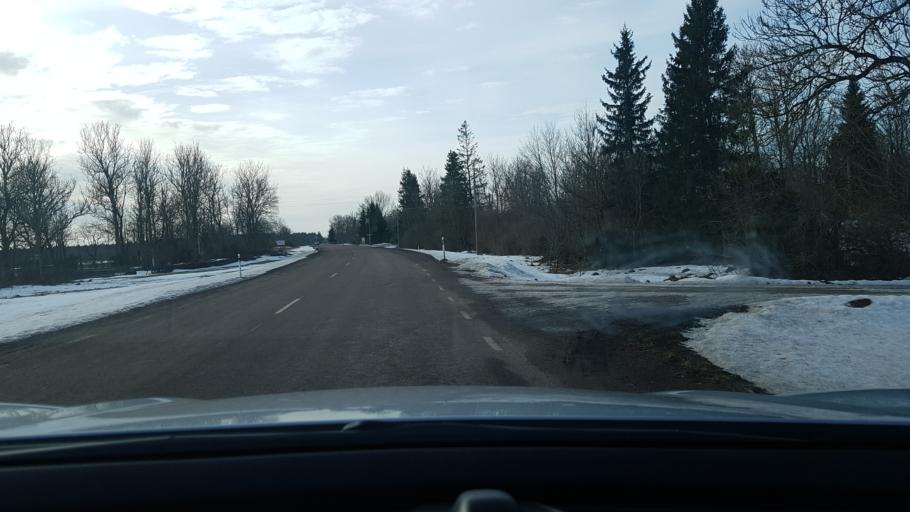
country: EE
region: Saare
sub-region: Kuressaare linn
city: Kuressaare
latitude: 58.3301
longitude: 22.5601
